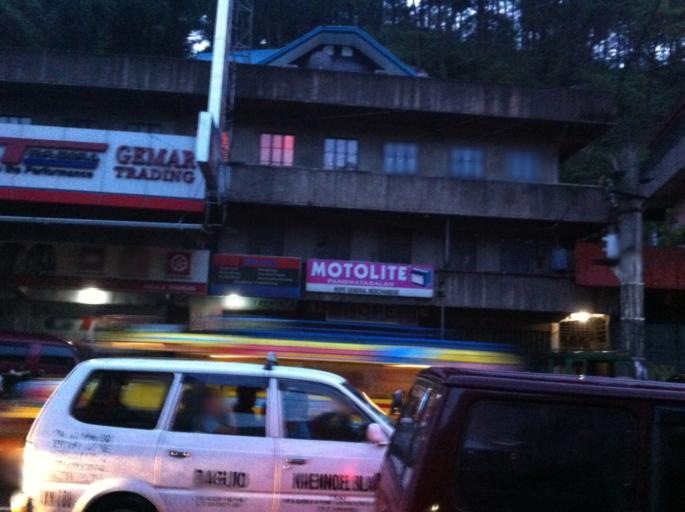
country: PH
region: Cordillera
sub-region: Province of Benguet
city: La Trinidad
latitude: 16.4412
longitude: 120.5937
